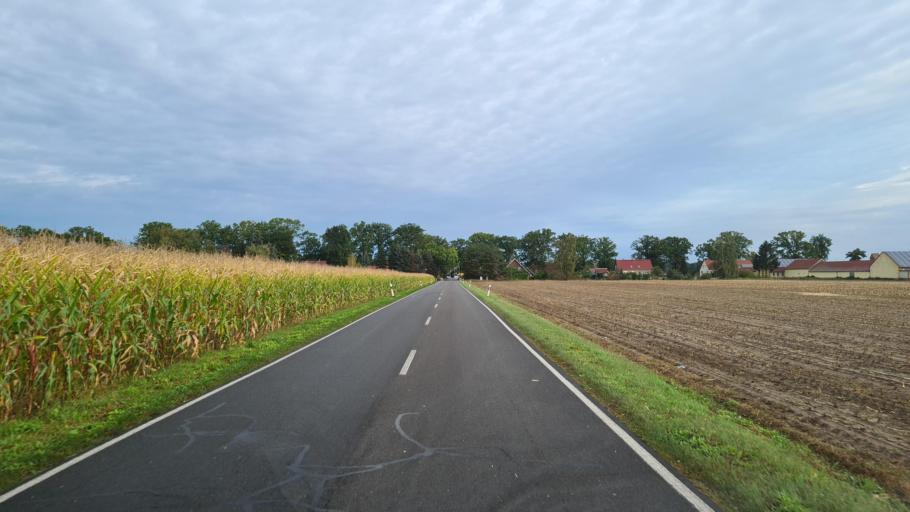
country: DE
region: Brandenburg
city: Kasel-Golzig
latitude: 51.9310
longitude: 13.7070
